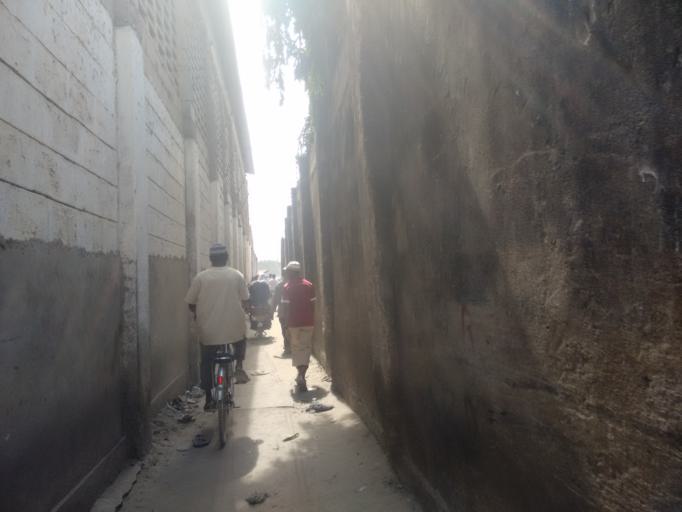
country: TZ
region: Dar es Salaam
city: Dar es Salaam
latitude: -6.8422
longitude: 39.2667
